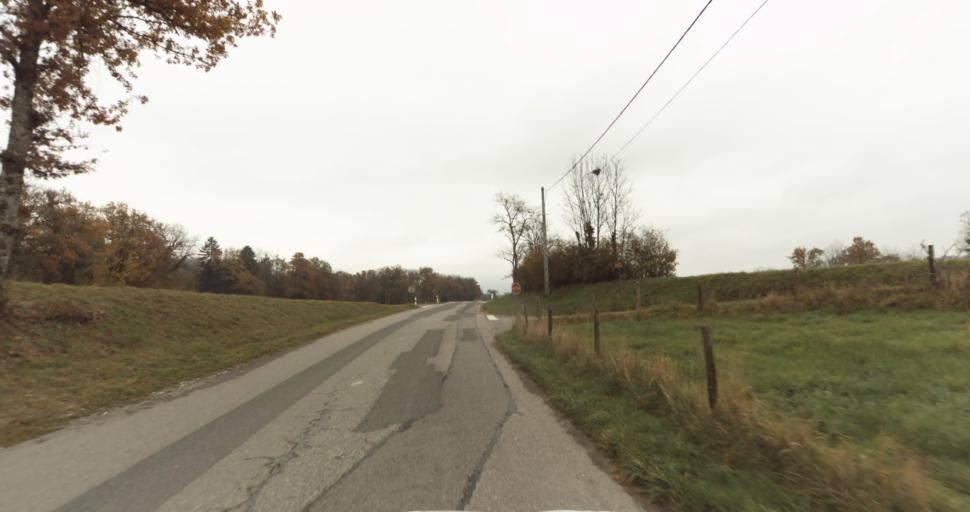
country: FR
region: Rhone-Alpes
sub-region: Departement de la Haute-Savoie
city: Alby-sur-Cheran
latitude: 45.8092
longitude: 6.0312
